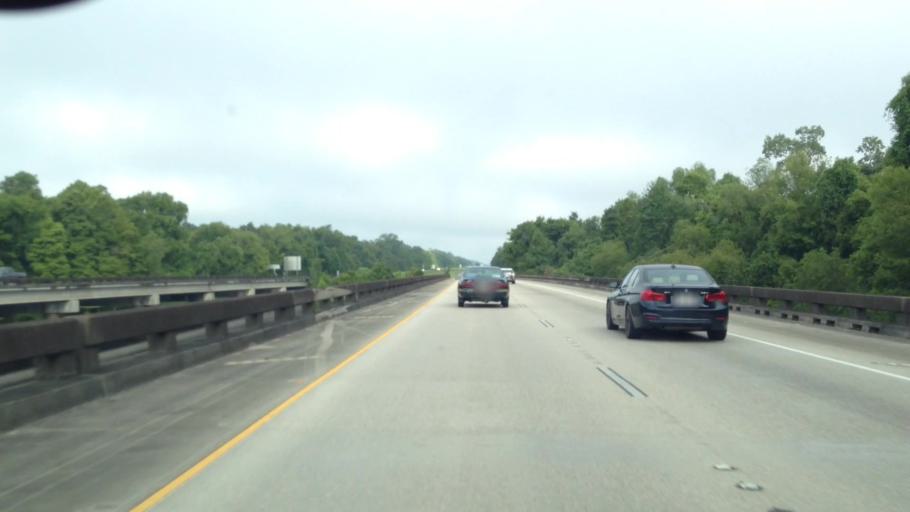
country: US
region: Louisiana
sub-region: Saint John the Baptist Parish
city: Reserve
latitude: 30.1128
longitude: -90.5616
